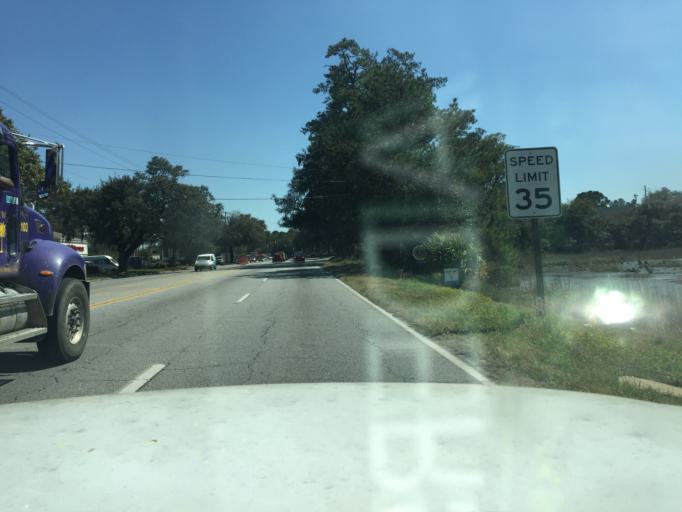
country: US
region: Georgia
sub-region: Chatham County
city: Wilmington Island
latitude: 32.0165
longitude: -80.9884
